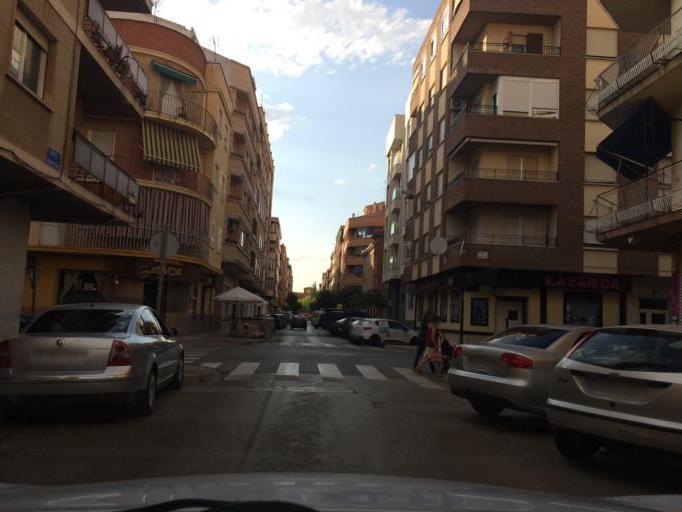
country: ES
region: Castille-La Mancha
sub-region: Provincia de Albacete
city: Albacete
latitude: 38.9906
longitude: -1.8624
